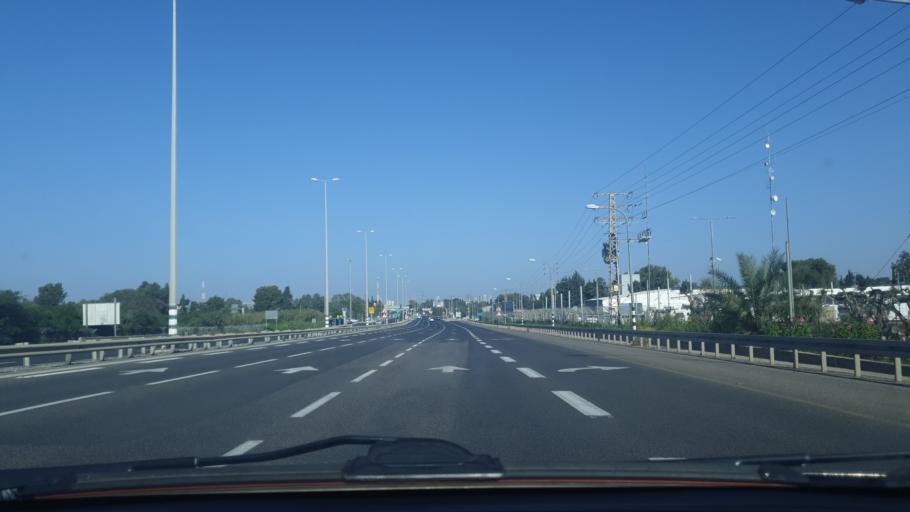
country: IL
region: Central District
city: Bet Dagan
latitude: 31.9985
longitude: 34.8230
